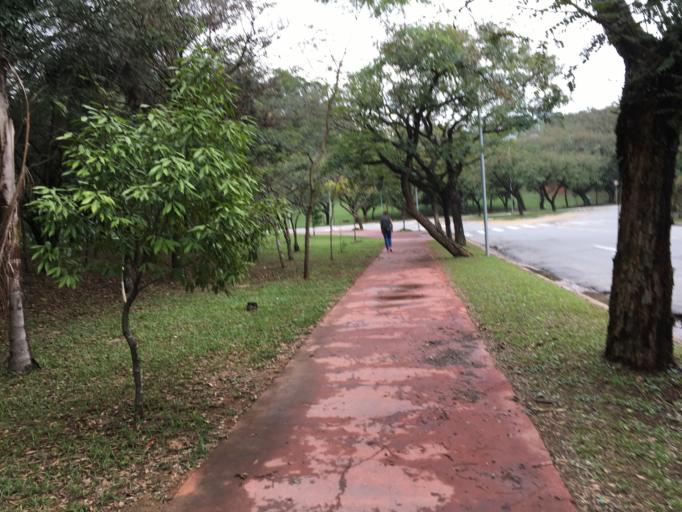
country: BR
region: Sao Paulo
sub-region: Osasco
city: Osasco
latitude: -23.5602
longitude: -46.7260
